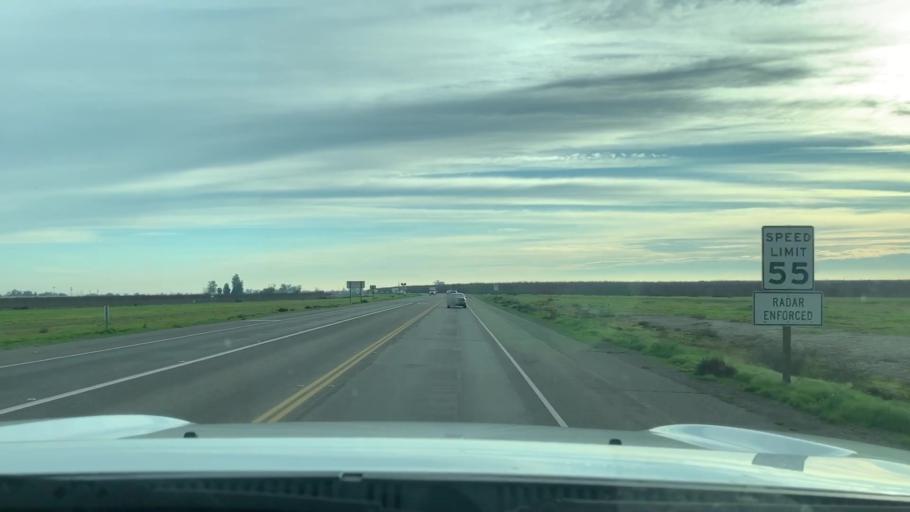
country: US
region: California
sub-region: Fresno County
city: Caruthers
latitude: 36.4883
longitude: -119.7902
